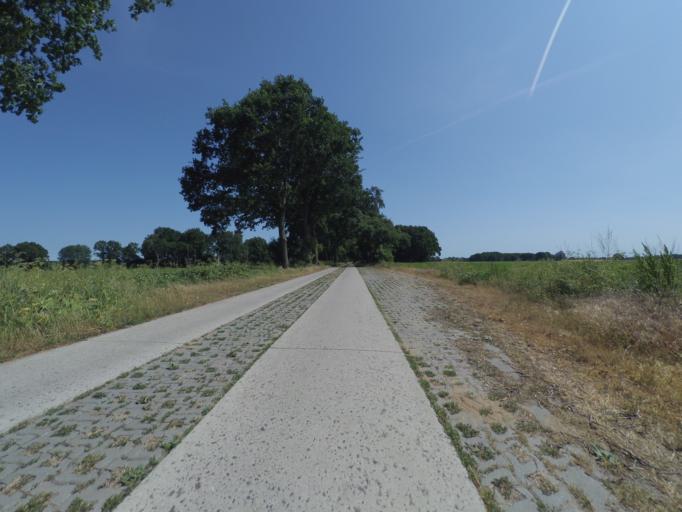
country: DE
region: Brandenburg
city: Heiligengrabe
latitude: 53.1953
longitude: 12.3225
